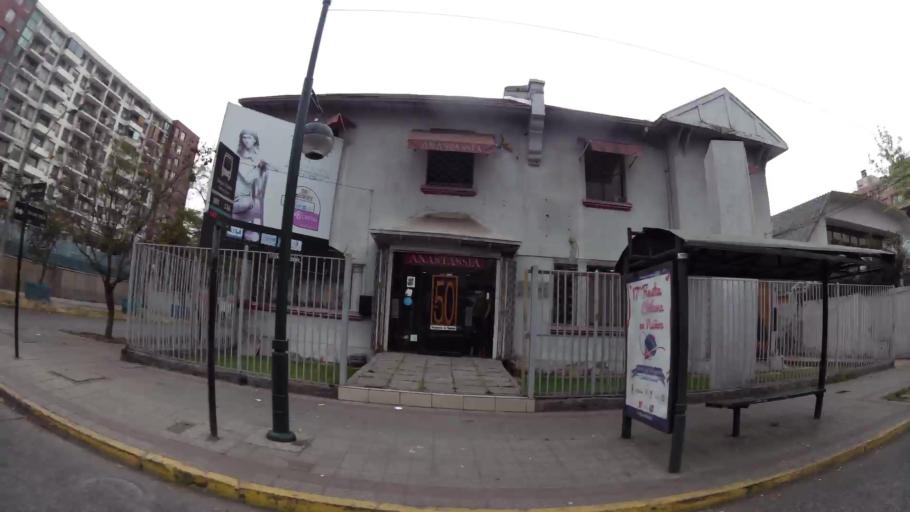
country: CL
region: Santiago Metropolitan
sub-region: Provincia de Santiago
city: Villa Presidente Frei, Nunoa, Santiago, Chile
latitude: -33.4510
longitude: -70.6130
